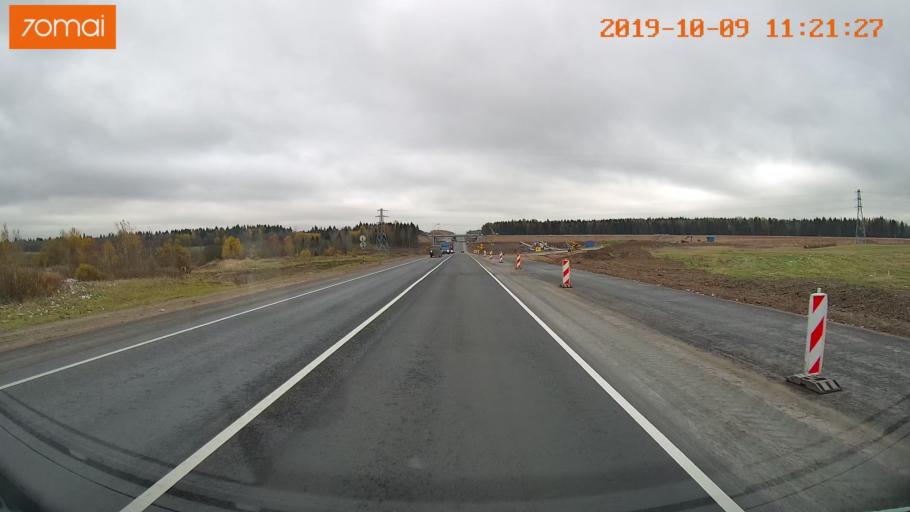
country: RU
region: Vologda
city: Vologda
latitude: 59.1395
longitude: 39.9494
